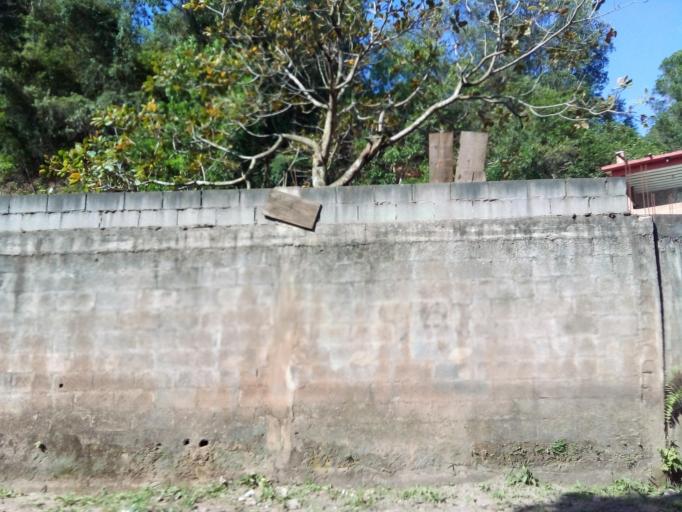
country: BR
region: Espirito Santo
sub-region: Vitoria
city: Vitoria
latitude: -20.2986
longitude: -40.3733
